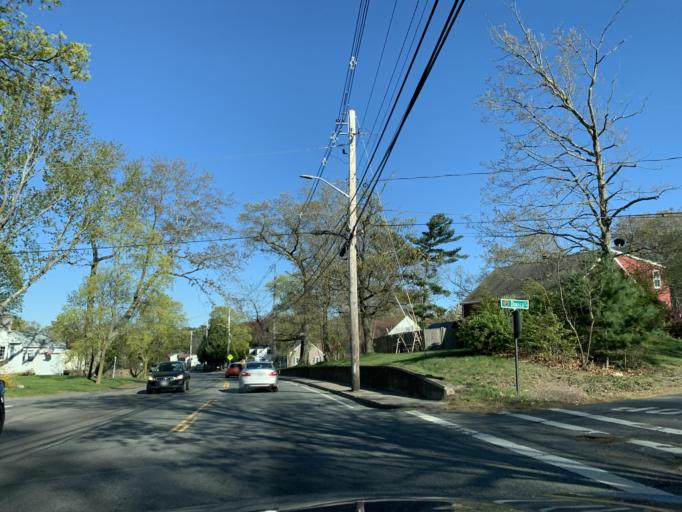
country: US
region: Massachusetts
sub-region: Norfolk County
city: Canton
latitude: 42.1344
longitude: -71.1436
